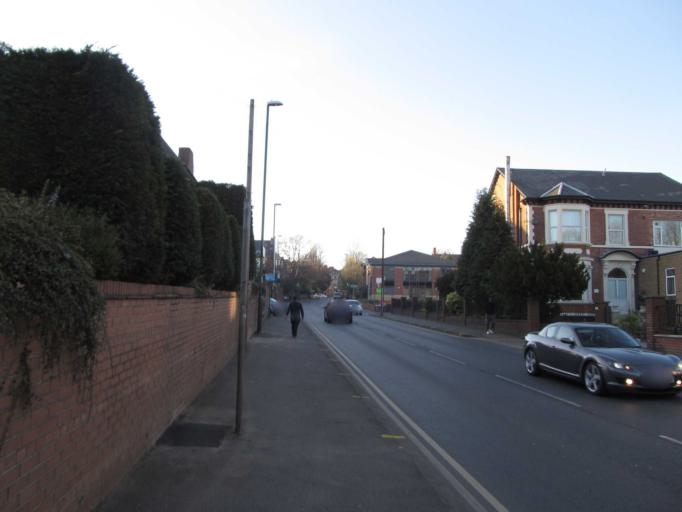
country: GB
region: England
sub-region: Nottingham
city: Nottingham
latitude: 52.9692
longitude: -1.1566
